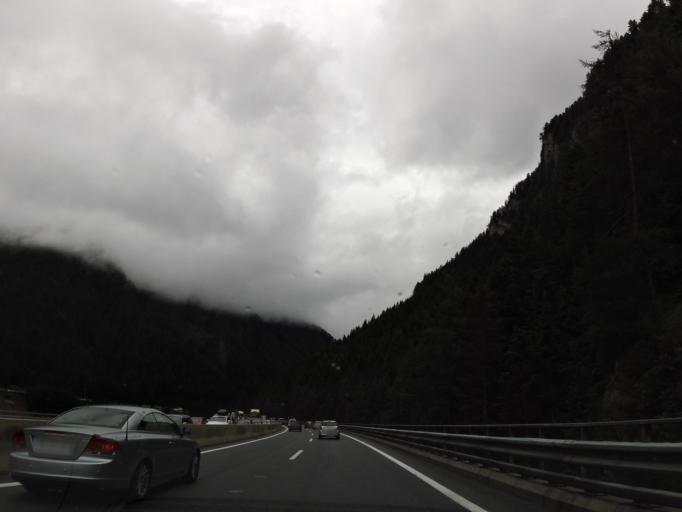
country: AT
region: Tyrol
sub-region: Politischer Bezirk Innsbruck Land
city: Gries am Brenner
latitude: 47.0267
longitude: 11.4926
